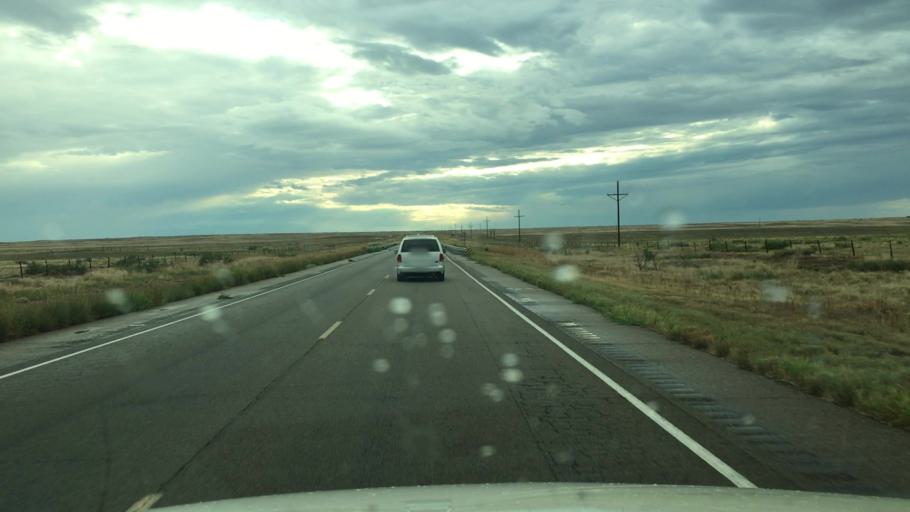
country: US
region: New Mexico
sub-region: Chaves County
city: Dexter
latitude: 33.4062
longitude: -104.3029
